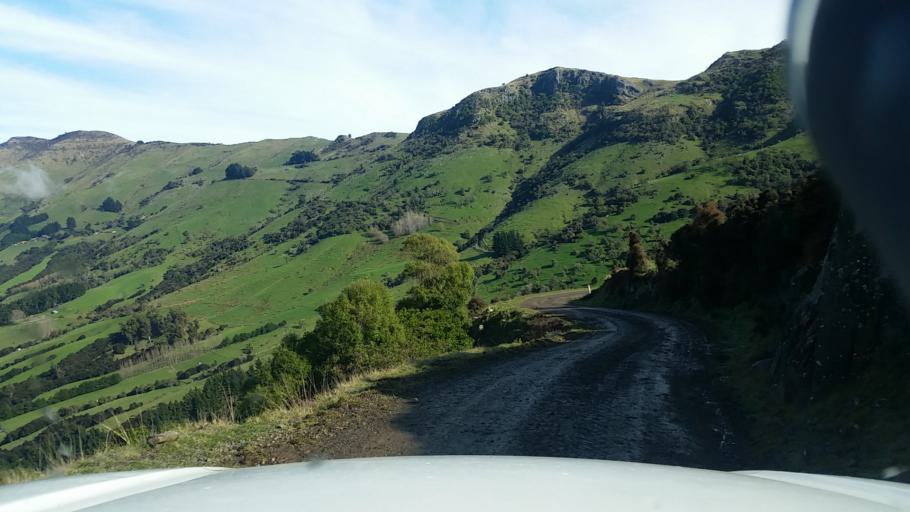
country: NZ
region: Canterbury
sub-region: Christchurch City
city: Christchurch
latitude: -43.6675
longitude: 172.8764
